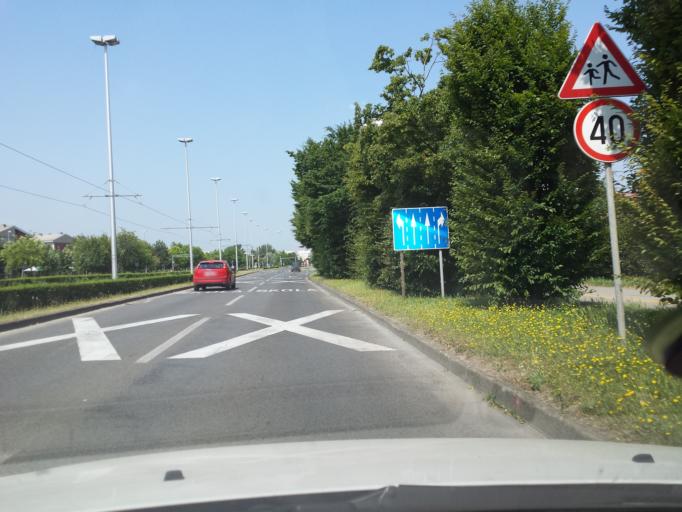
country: HR
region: Grad Zagreb
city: Jankomir
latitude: 45.7888
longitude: 15.9249
